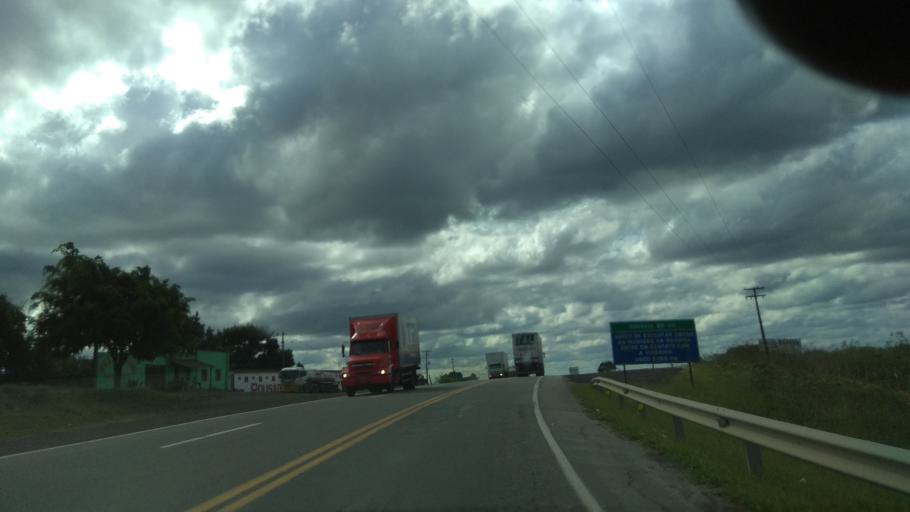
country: BR
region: Bahia
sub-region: Santa Ines
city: Santa Ines
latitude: -13.0929
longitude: -39.9632
